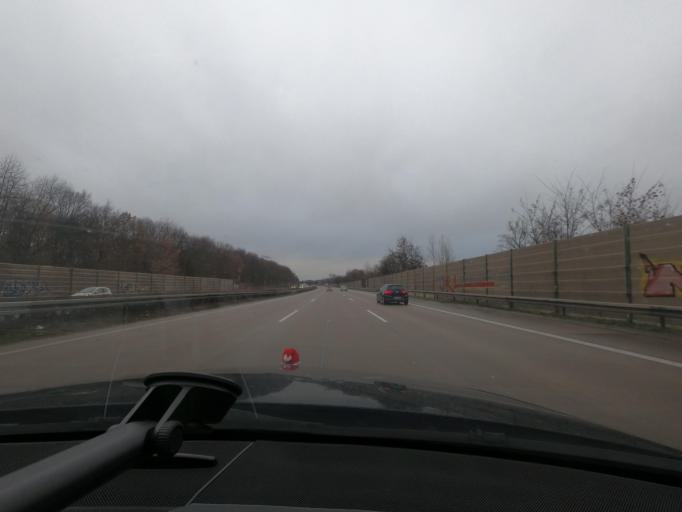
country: DE
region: Lower Saxony
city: Hildesheim
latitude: 52.1703
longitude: 9.9832
